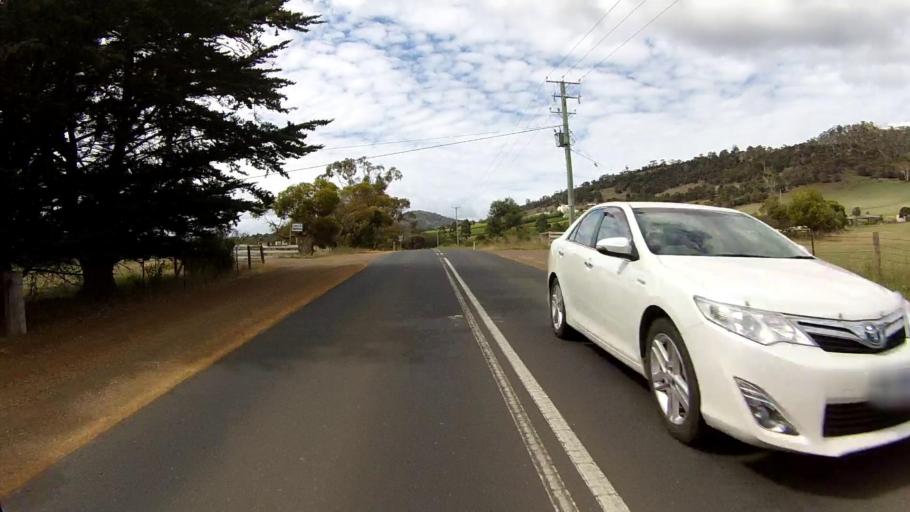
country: AU
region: Tasmania
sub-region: Clarence
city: Cambridge
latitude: -42.7941
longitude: 147.4193
